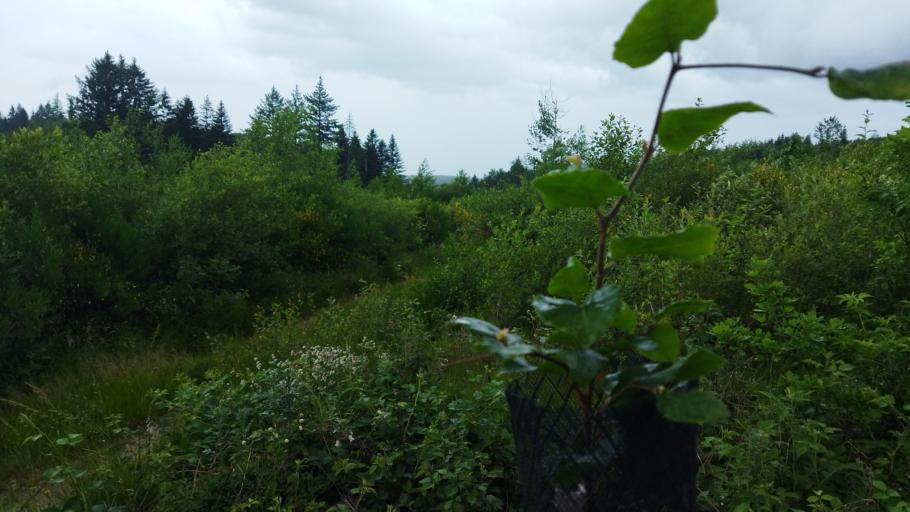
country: FR
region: Limousin
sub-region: Departement de la Creuse
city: Banize
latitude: 45.7865
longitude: 1.9933
